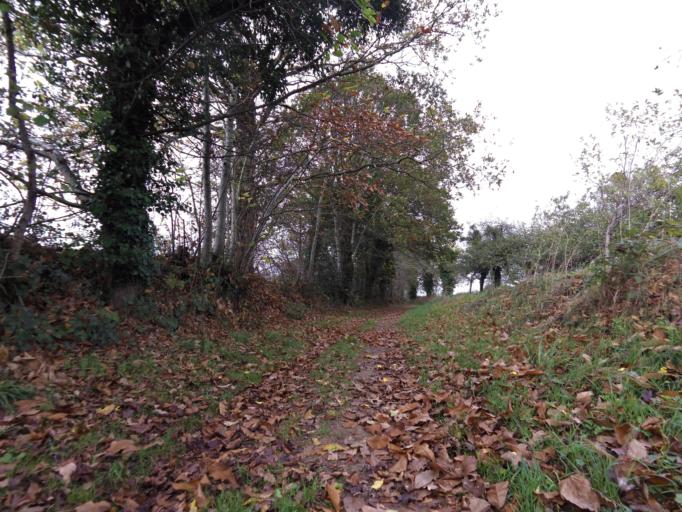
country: FR
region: Brittany
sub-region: Departement d'Ille-et-Vilaine
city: Chanteloup
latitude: 47.9664
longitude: -1.6514
